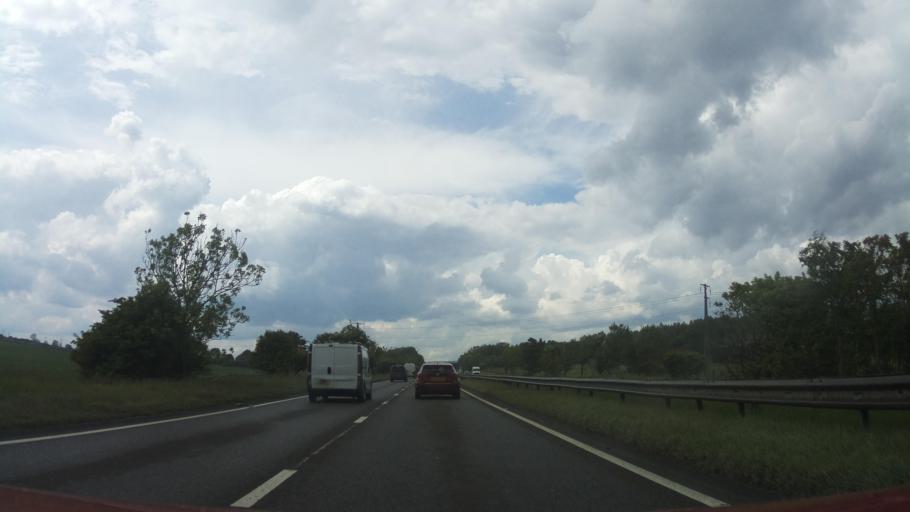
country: GB
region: England
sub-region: County Durham
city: Murton
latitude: 54.8533
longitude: -1.4101
